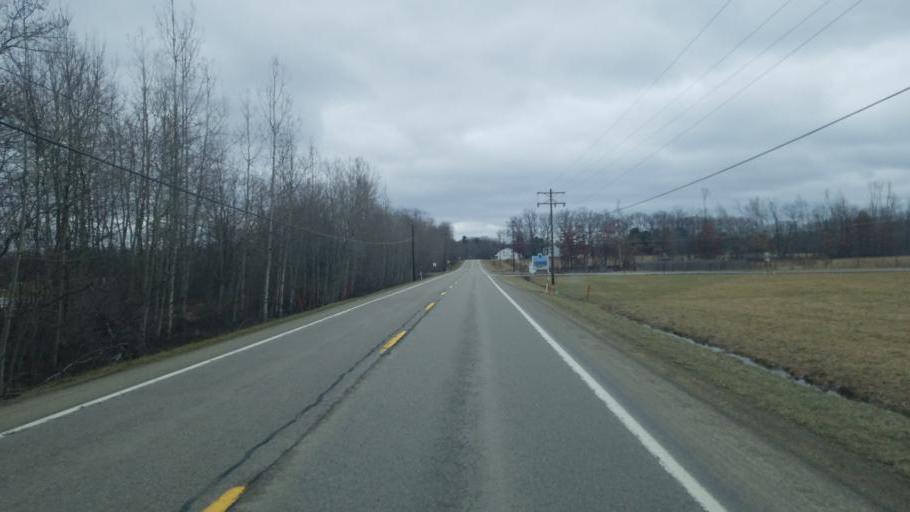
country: US
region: Pennsylvania
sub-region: Forest County
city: Marienville
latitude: 41.3940
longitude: -79.2608
